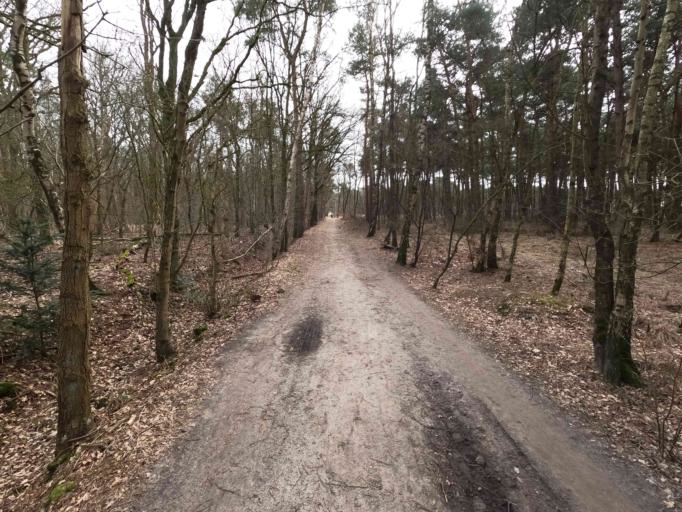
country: BE
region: Flanders
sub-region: Provincie Antwerpen
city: Kalmthout
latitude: 51.3995
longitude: 4.4467
